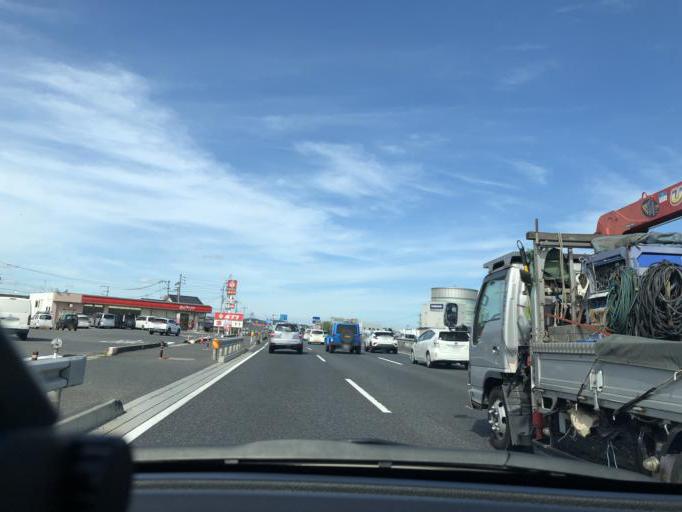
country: JP
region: Okayama
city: Kurashiki
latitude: 34.5906
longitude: 133.7974
